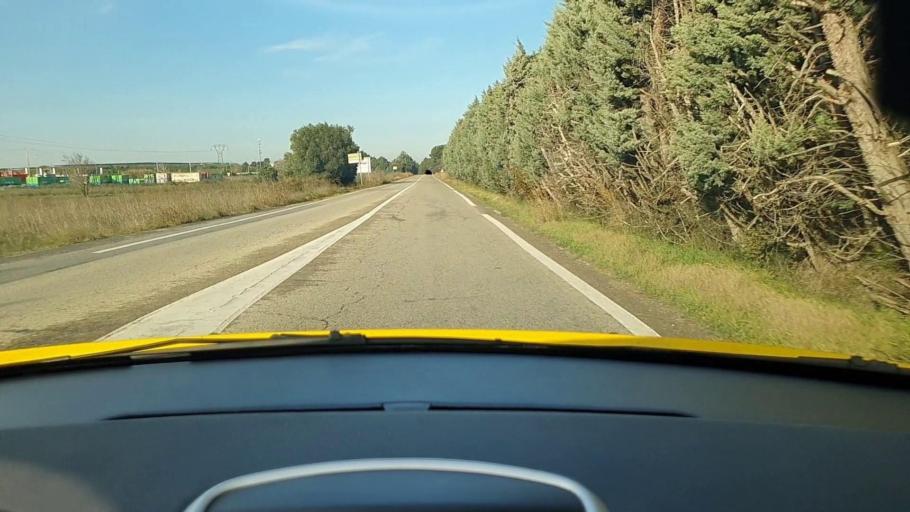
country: FR
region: Languedoc-Roussillon
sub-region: Departement du Gard
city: Comps
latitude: 43.8219
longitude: 4.5998
